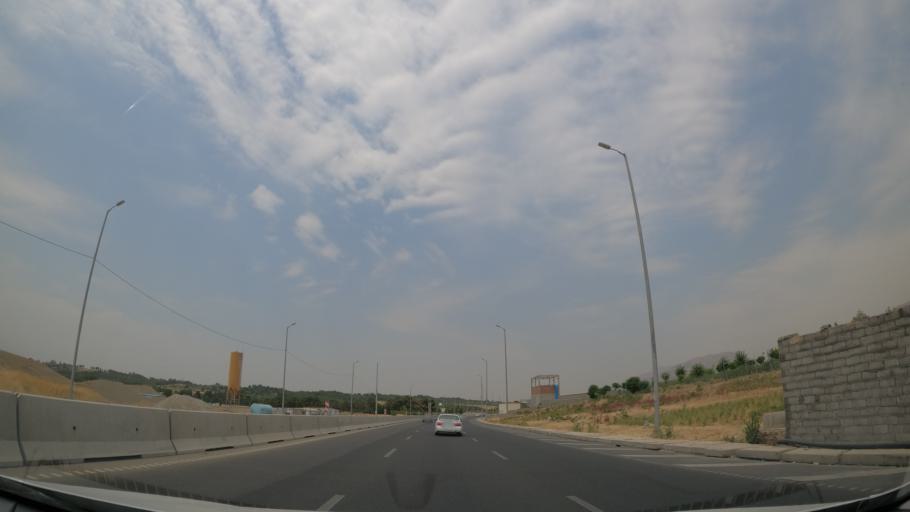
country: IR
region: Tehran
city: Shahr-e Qods
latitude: 35.7390
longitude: 51.2213
